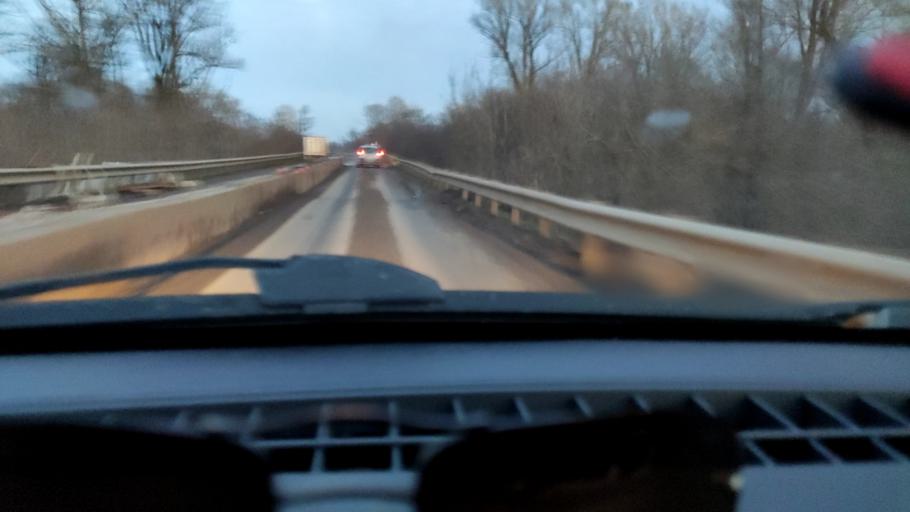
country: RU
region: Bashkortostan
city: Ufa
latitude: 54.5688
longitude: 55.9767
